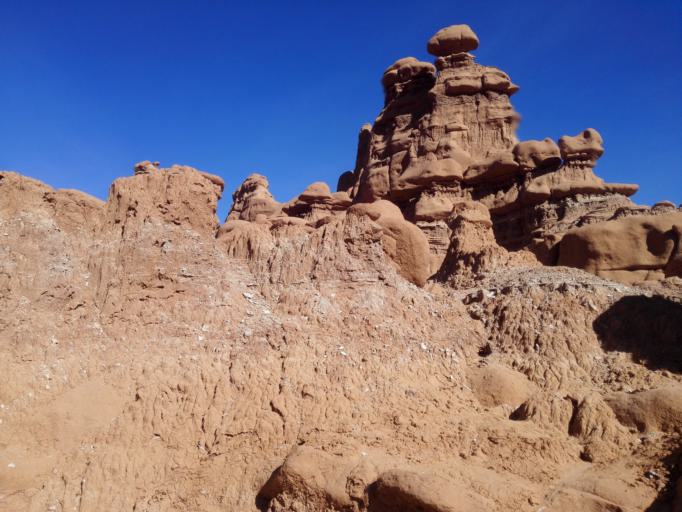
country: US
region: Utah
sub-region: Emery County
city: Ferron
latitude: 38.5580
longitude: -110.7000
